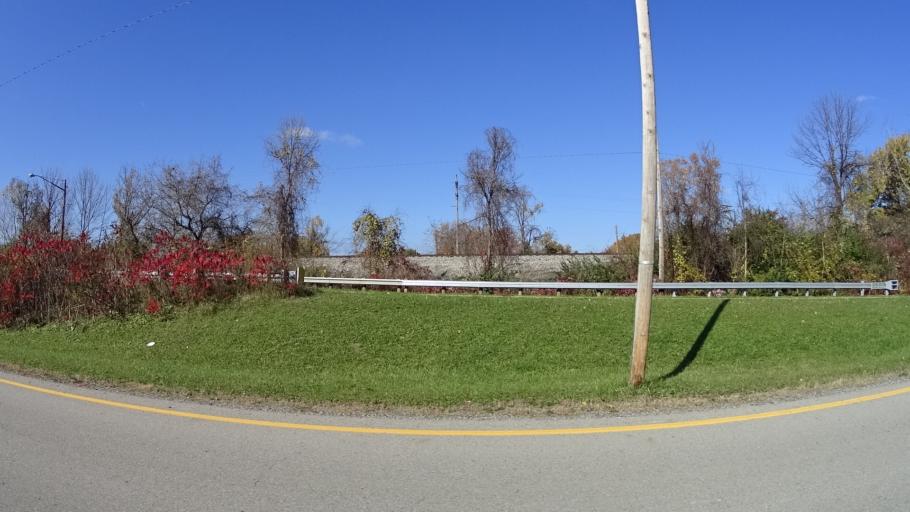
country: US
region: Ohio
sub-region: Lorain County
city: Lorain
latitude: 41.4475
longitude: -82.2217
